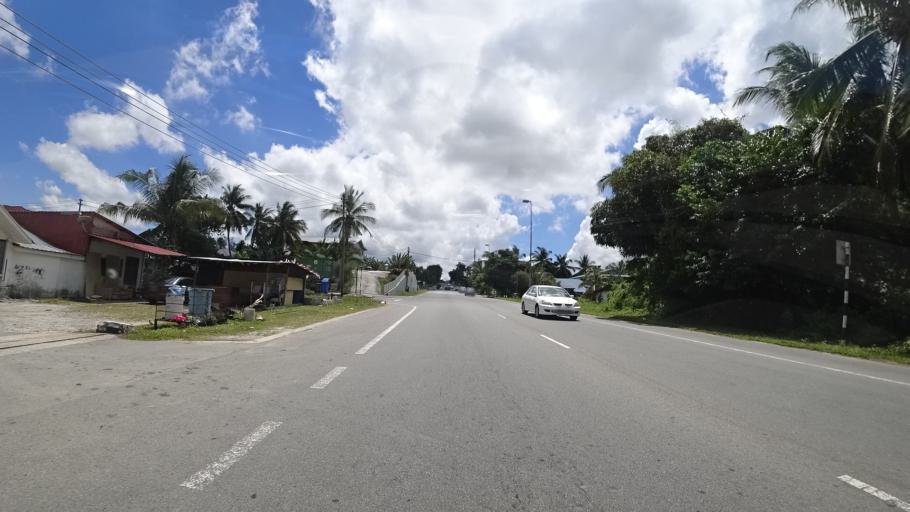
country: BN
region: Brunei and Muara
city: Bandar Seri Begawan
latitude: 4.9416
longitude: 114.9547
